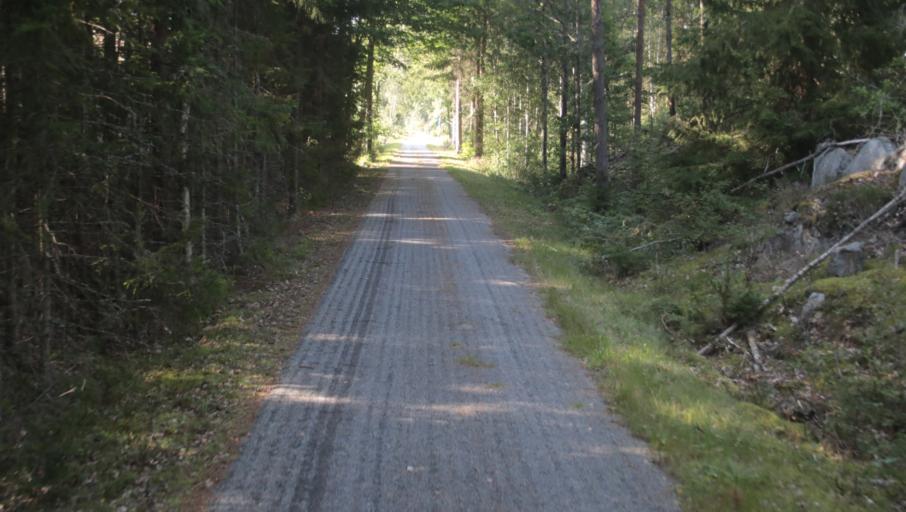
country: SE
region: Blekinge
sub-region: Karlshamns Kommun
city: Svangsta
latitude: 56.3176
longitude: 14.7088
